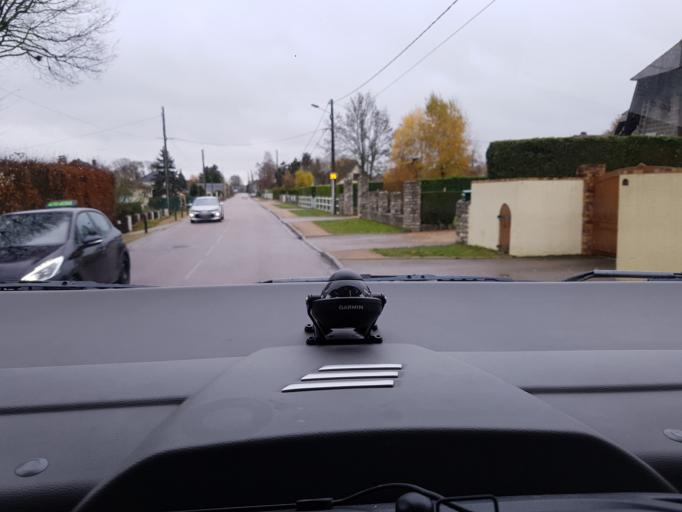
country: FR
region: Haute-Normandie
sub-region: Departement de l'Eure
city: Pont-Saint-Pierre
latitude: 49.3167
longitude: 1.3016
